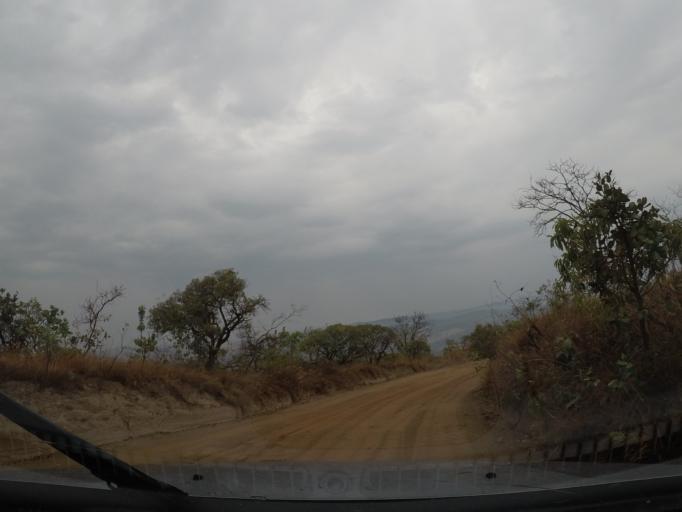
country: BR
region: Goias
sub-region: Pirenopolis
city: Pirenopolis
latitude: -15.8294
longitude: -48.9042
